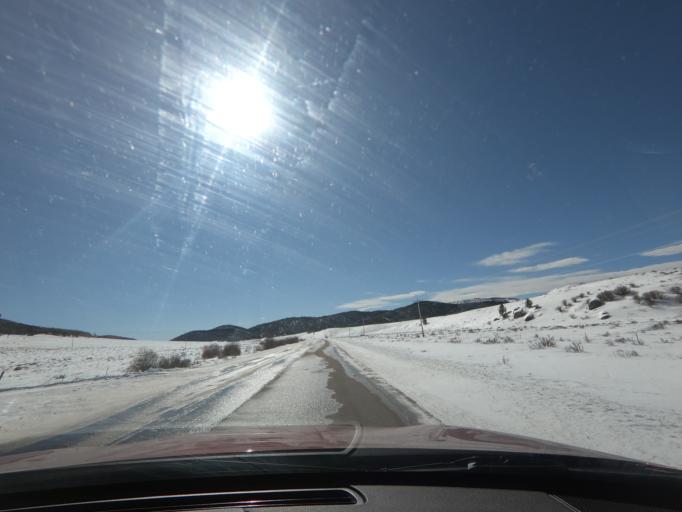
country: US
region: Colorado
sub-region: Teller County
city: Cripple Creek
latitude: 38.7765
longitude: -105.1220
